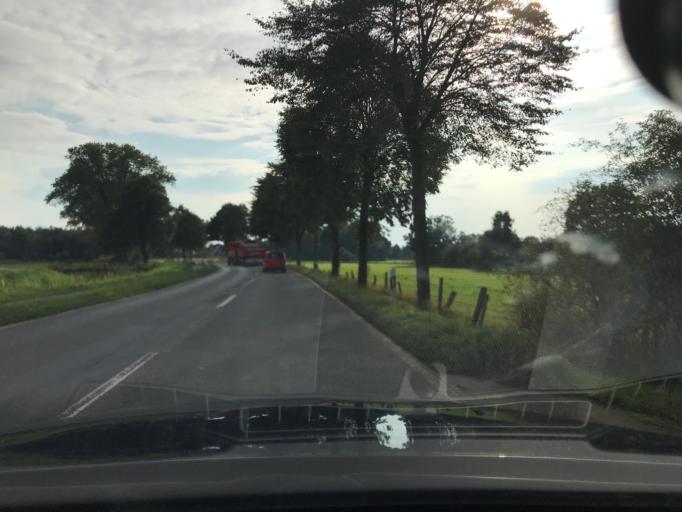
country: DE
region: Lower Saxony
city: Riede
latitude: 52.9911
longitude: 8.8953
